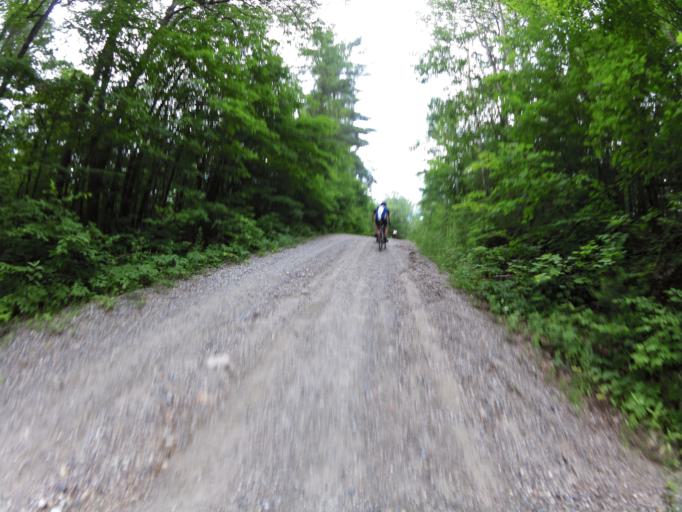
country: CA
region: Ontario
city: Perth
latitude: 45.0128
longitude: -76.5852
